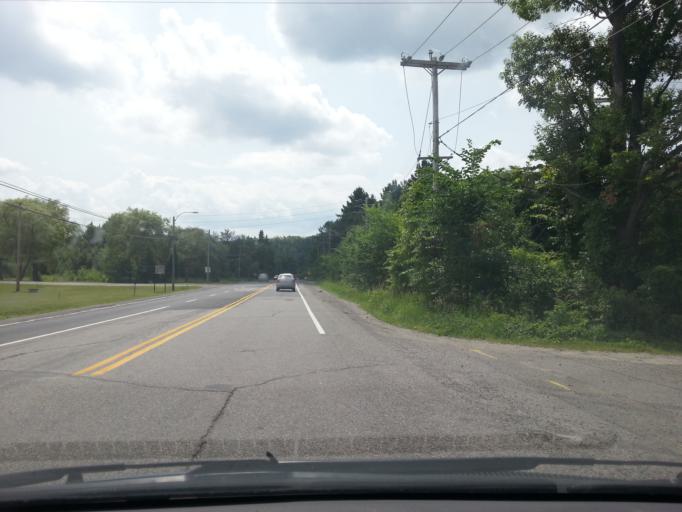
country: CA
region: Quebec
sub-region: Outaouais
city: Gatineau
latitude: 45.4982
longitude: -75.7618
